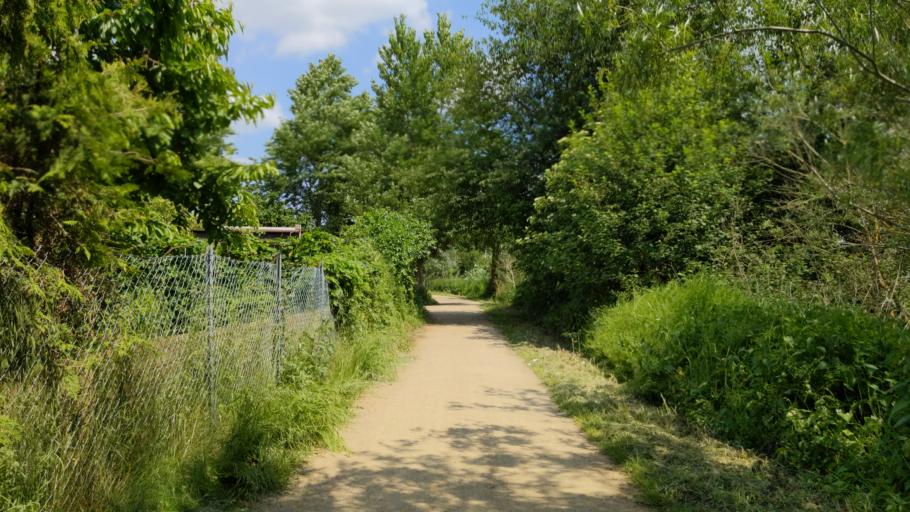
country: DE
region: Schleswig-Holstein
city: Luebeck
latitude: 53.8513
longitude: 10.6700
